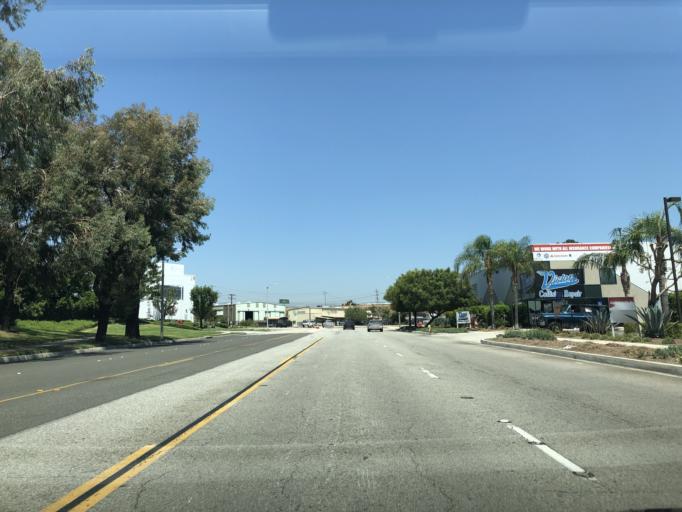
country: US
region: California
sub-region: San Bernardino County
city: Rancho Cucamonga
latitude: 34.0895
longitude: -117.5472
